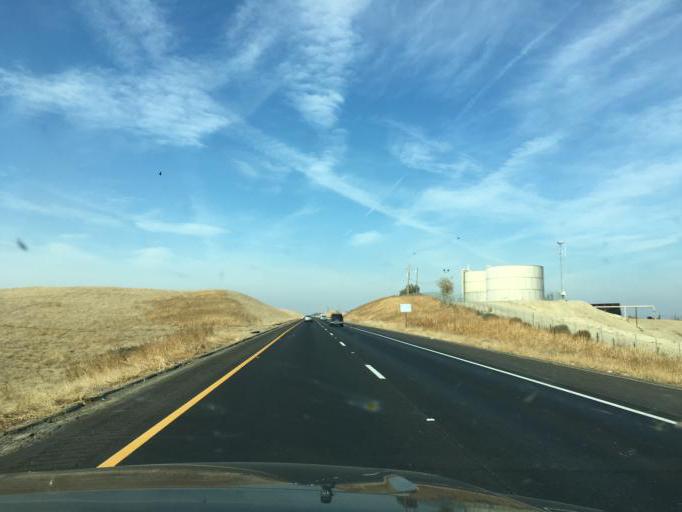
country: US
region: California
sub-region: Fresno County
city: Coalinga
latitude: 36.3051
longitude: -120.2770
